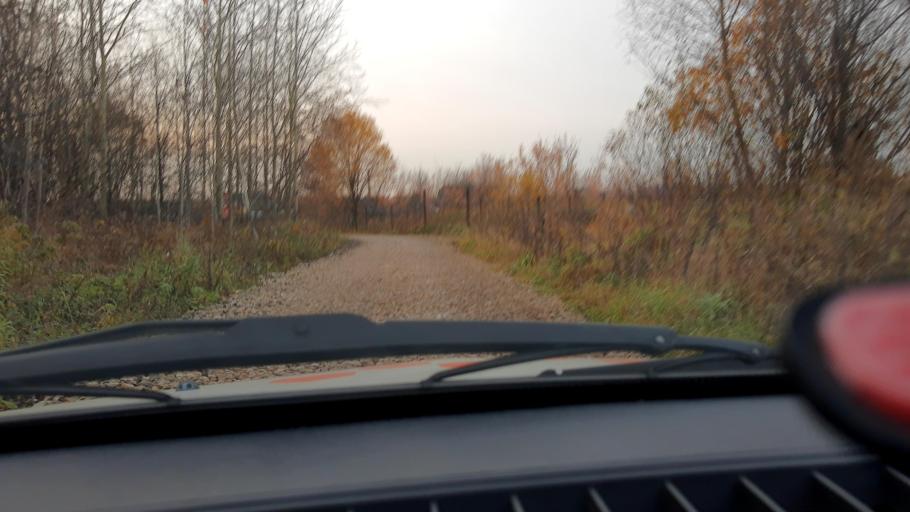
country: RU
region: Bashkortostan
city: Iglino
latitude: 54.7980
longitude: 56.3440
